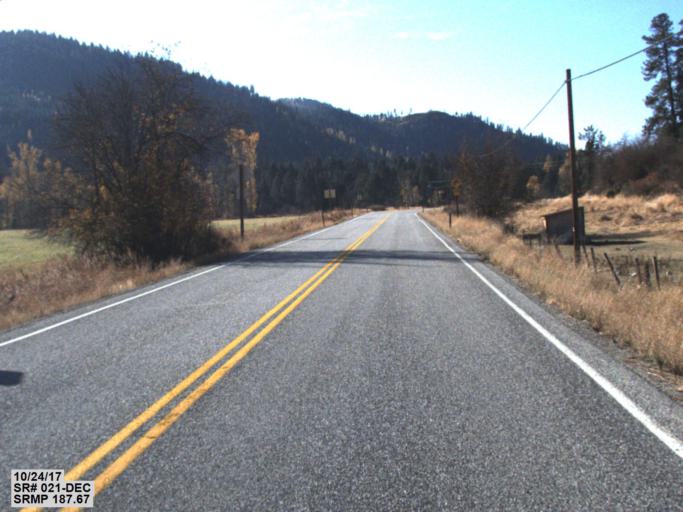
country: CA
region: British Columbia
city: Grand Forks
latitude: 48.9580
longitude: -118.5348
